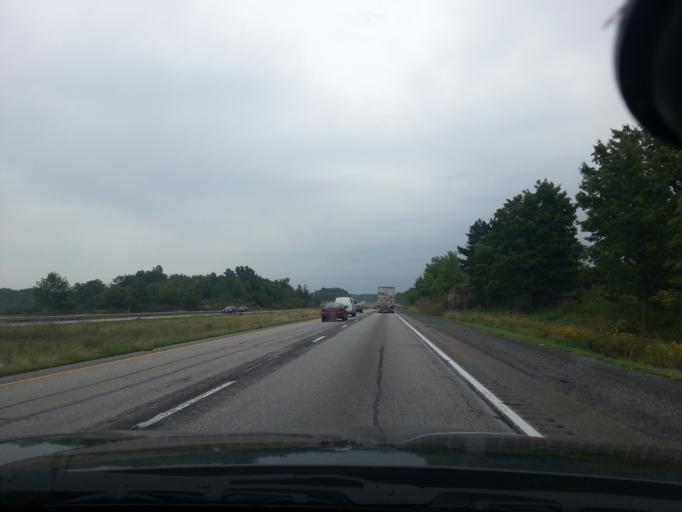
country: CA
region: Ontario
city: Gananoque
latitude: 44.3471
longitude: -76.1188
